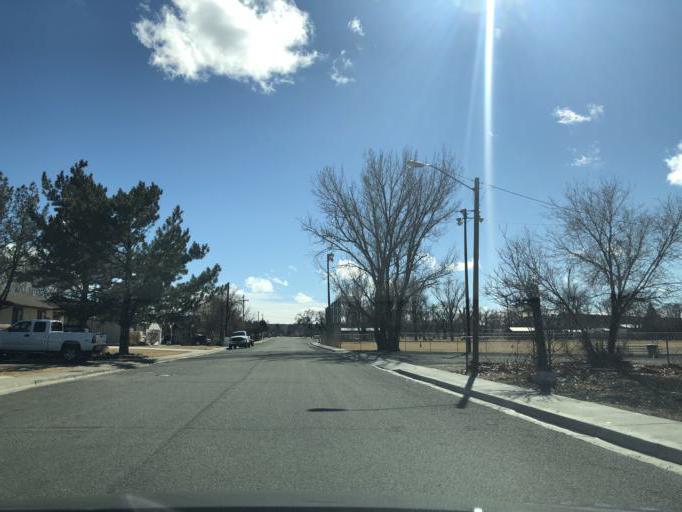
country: US
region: Utah
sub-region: Carbon County
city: East Carbon City
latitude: 38.9983
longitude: -110.1599
